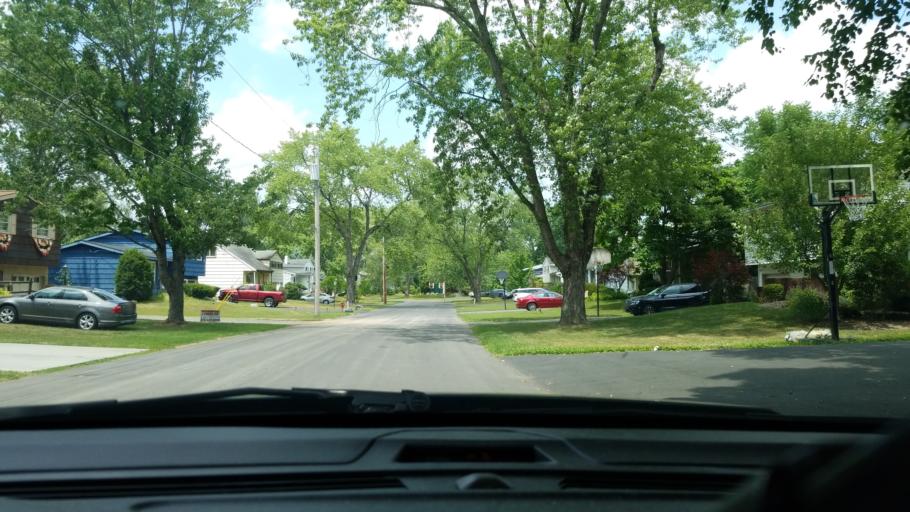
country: US
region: New York
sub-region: Onondaga County
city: Liverpool
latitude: 43.1395
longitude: -76.2138
